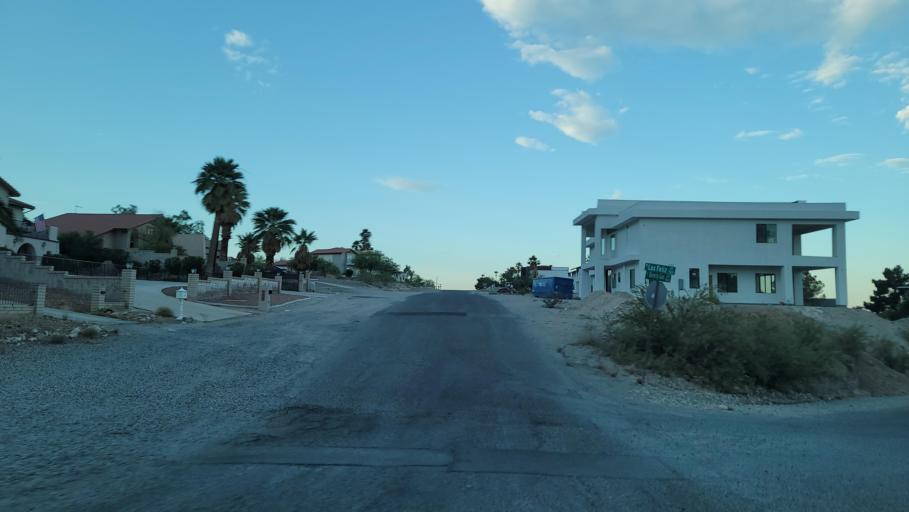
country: US
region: Nevada
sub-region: Clark County
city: Sunrise Manor
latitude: 36.1729
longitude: -115.0168
